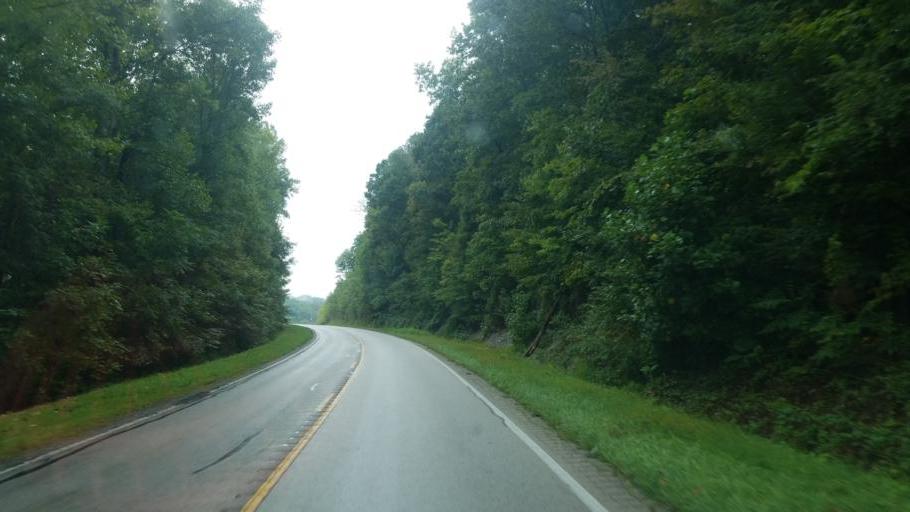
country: US
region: Kentucky
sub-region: Rowan County
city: Morehead
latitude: 38.1512
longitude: -83.5020
